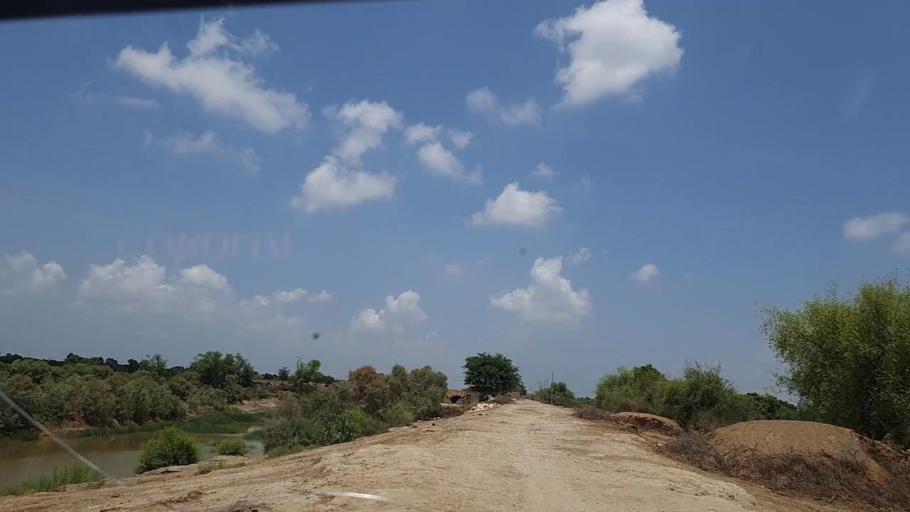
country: PK
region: Sindh
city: Tharu Shah
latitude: 26.9205
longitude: 67.9895
